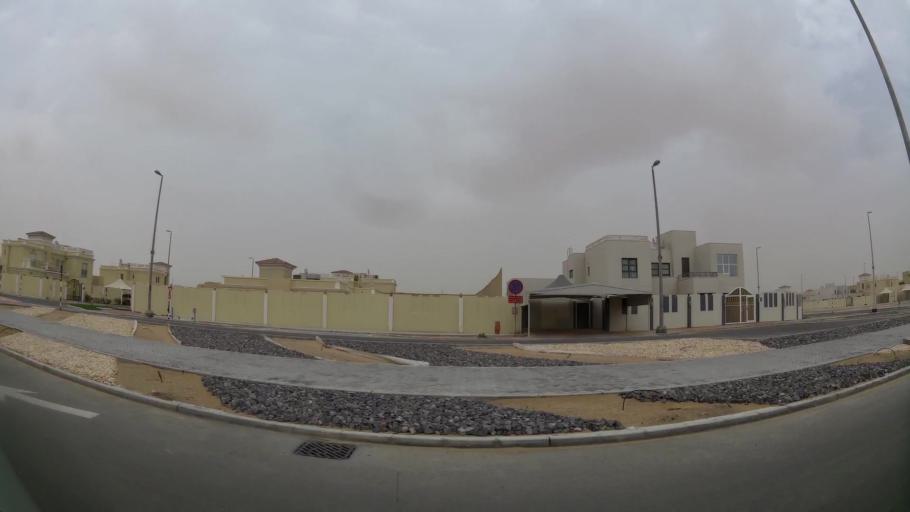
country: AE
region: Abu Dhabi
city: Abu Dhabi
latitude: 24.4481
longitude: 54.7369
